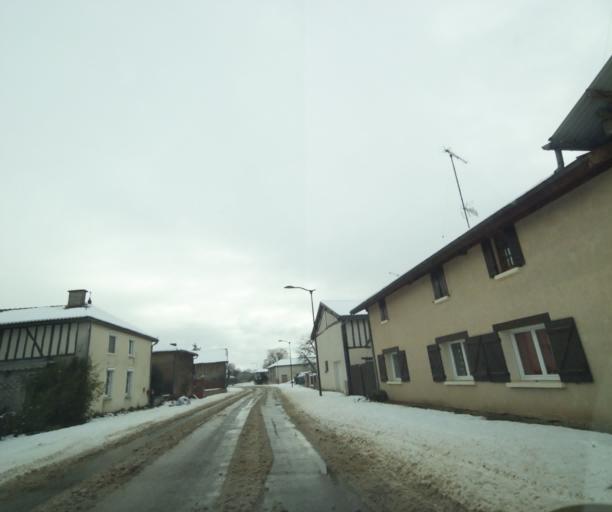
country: FR
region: Champagne-Ardenne
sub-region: Departement de la Haute-Marne
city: Montier-en-Der
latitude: 48.4384
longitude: 4.7122
